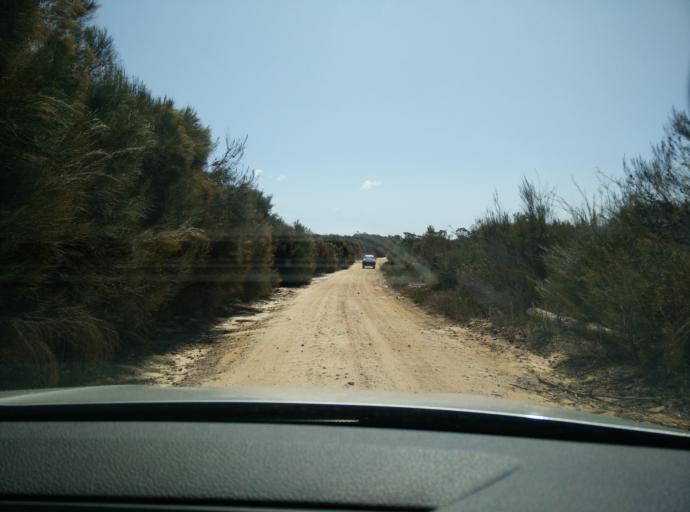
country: AU
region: New South Wales
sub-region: Gosford Shire
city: Umina
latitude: -33.5488
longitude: 151.2873
